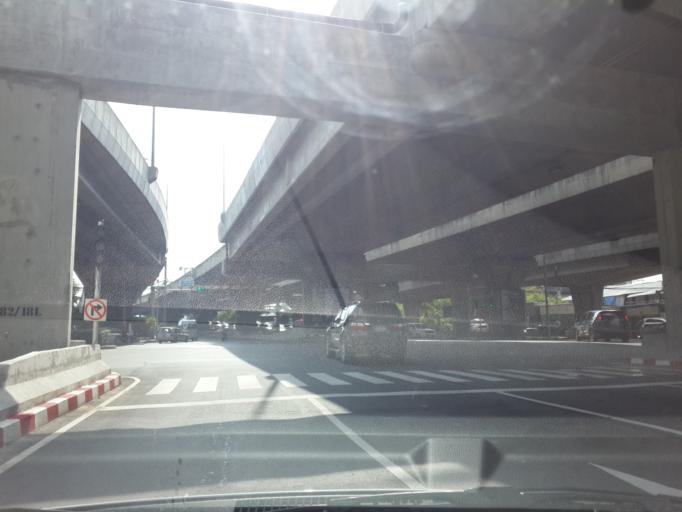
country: TH
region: Bangkok
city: Din Daeng
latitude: 13.7525
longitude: 100.5692
